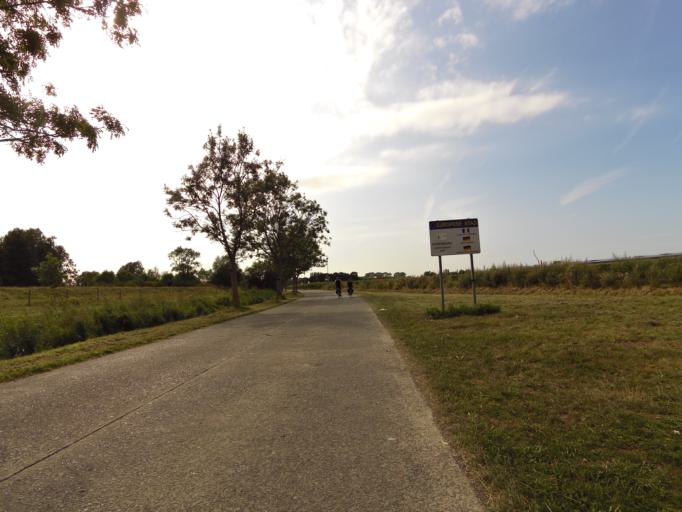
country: BE
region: Flanders
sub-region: Provincie West-Vlaanderen
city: Jabbeke
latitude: 51.1783
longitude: 3.0520
